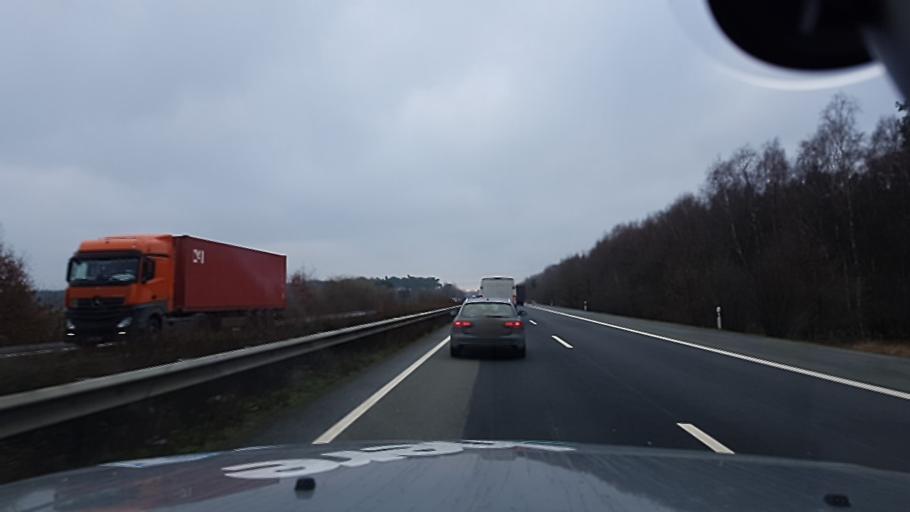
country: DE
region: Lower Saxony
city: Rieste
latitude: 52.4564
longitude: 8.0440
